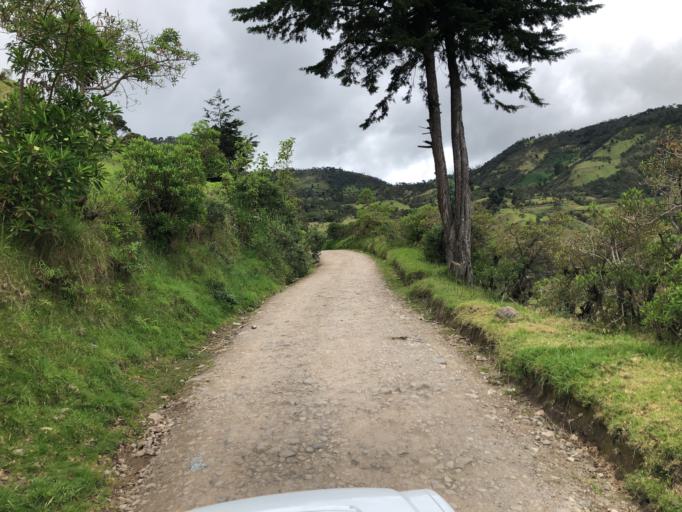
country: CO
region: Cauca
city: Totoro
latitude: 2.5112
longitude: -76.3699
